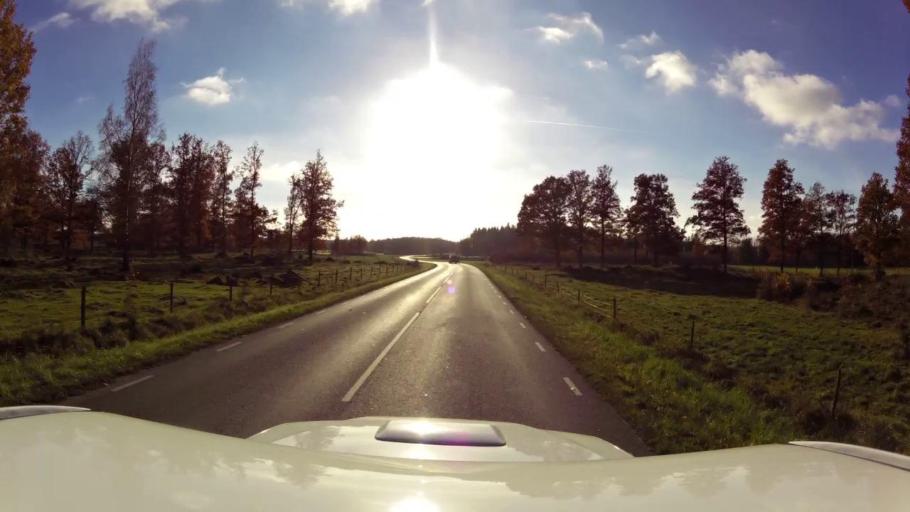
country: SE
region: OEstergoetland
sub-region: Linkopings Kommun
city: Malmslatt
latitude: 58.3326
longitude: 15.5128
